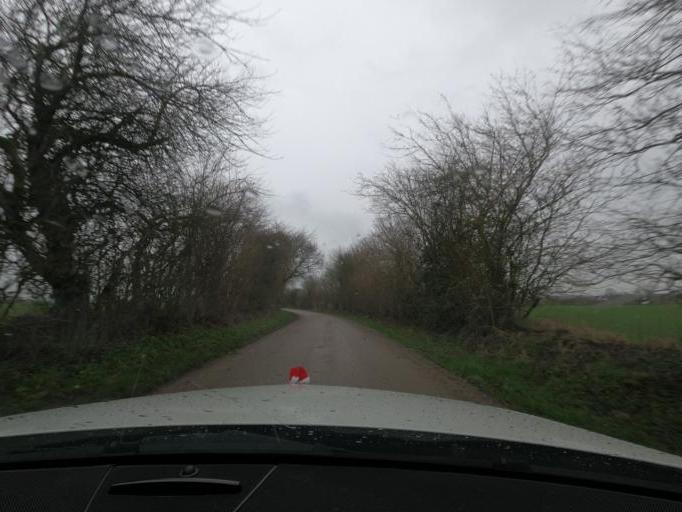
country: DK
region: South Denmark
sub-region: Haderslev Kommune
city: Starup
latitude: 55.2274
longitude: 9.5120
